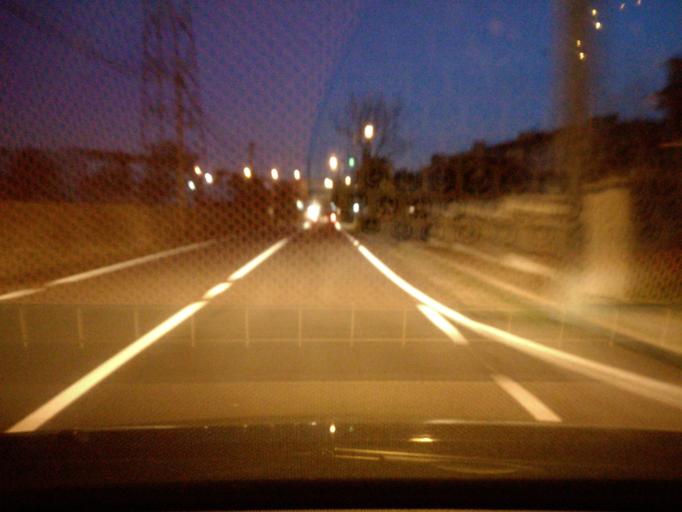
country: PT
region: Porto
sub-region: Maia
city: Maia
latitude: 41.2430
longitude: -8.6381
